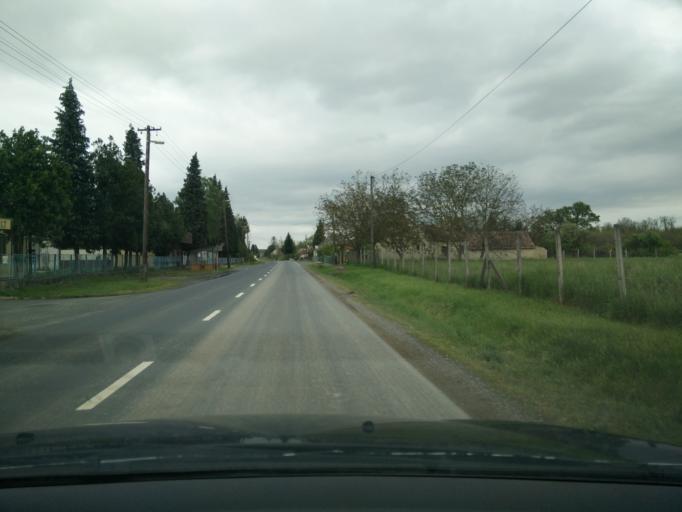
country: HU
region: Zala
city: Turje
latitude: 46.9863
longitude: 17.0780
